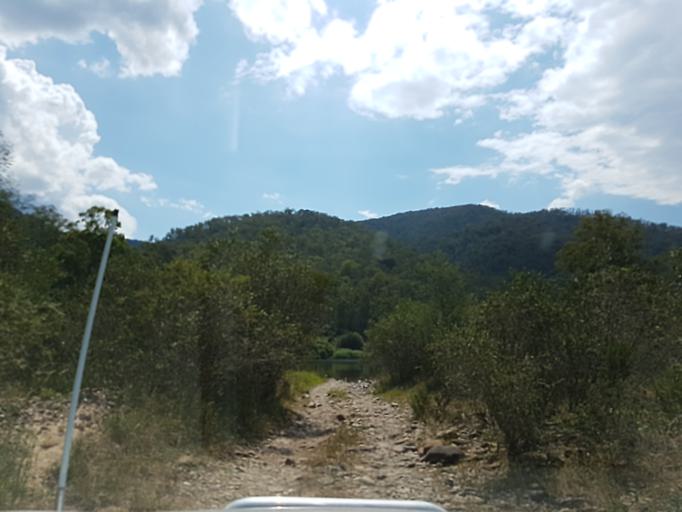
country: AU
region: Victoria
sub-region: East Gippsland
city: Lakes Entrance
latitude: -37.3949
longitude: 148.3345
